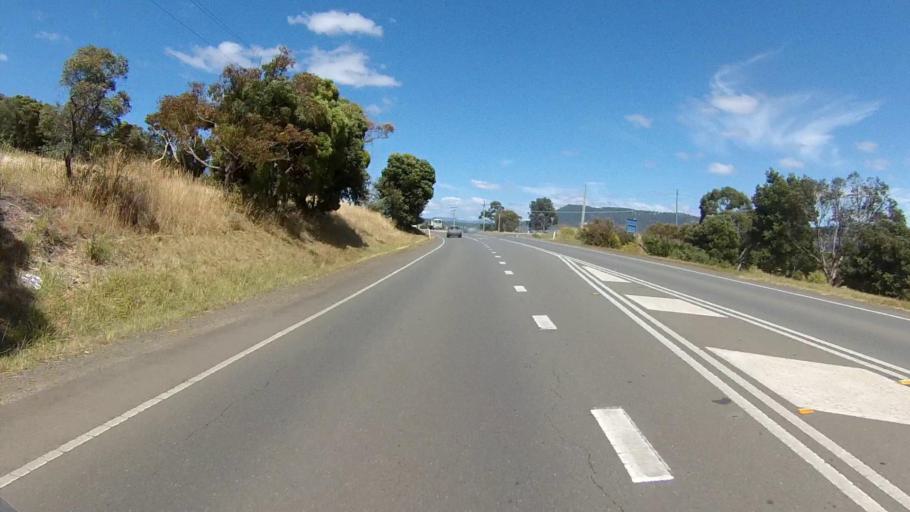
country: AU
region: Tasmania
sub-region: Clarence
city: Cambridge
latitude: -42.7422
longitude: 147.4210
